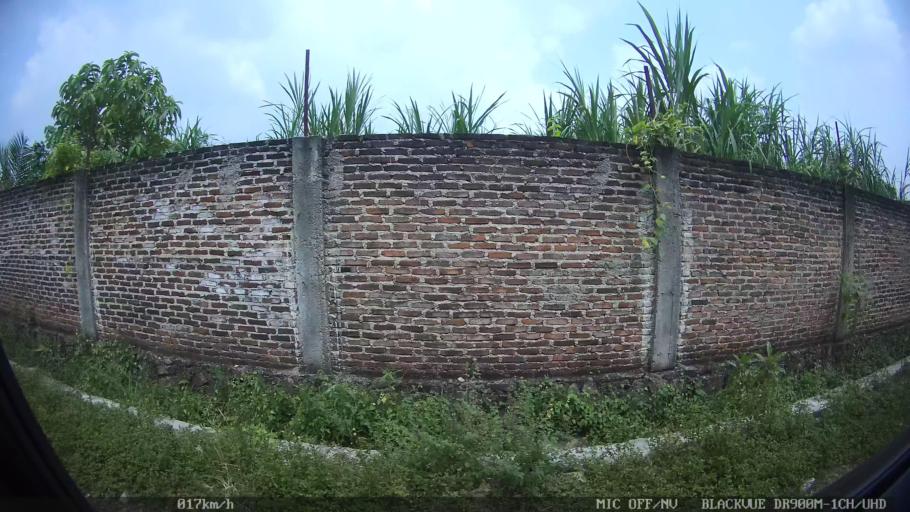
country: ID
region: Lampung
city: Gadingrejo
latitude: -5.3663
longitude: 105.0589
